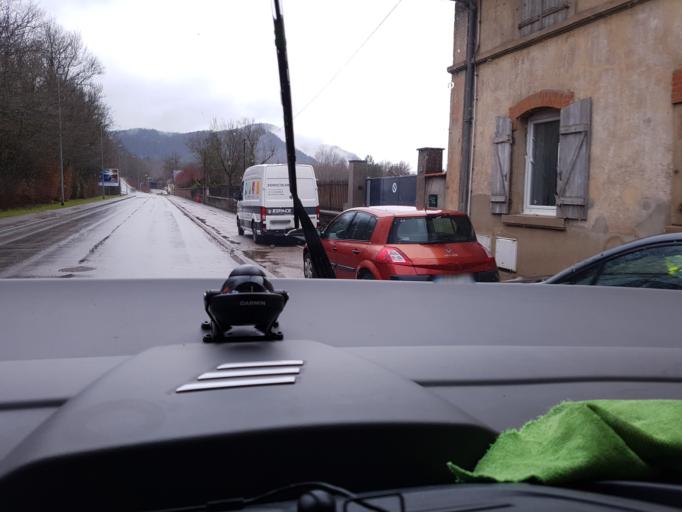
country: FR
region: Lorraine
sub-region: Departement des Vosges
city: Saint-Die-des-Vosges
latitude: 48.2851
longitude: 6.9389
